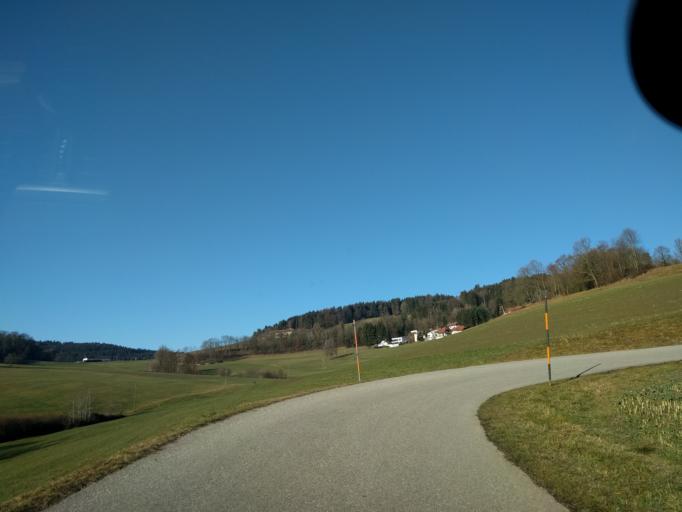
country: AT
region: Upper Austria
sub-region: Politischer Bezirk Urfahr-Umgebung
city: Kirchschlag bei Linz
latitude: 48.3963
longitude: 14.2888
